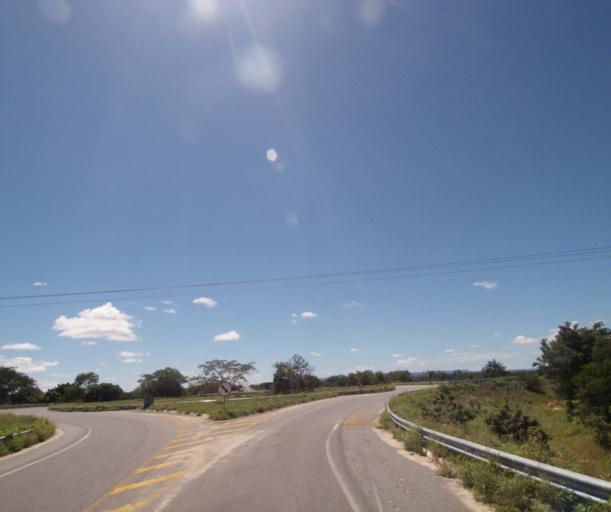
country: BR
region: Bahia
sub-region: Carinhanha
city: Carinhanha
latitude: -14.3193
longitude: -43.7804
